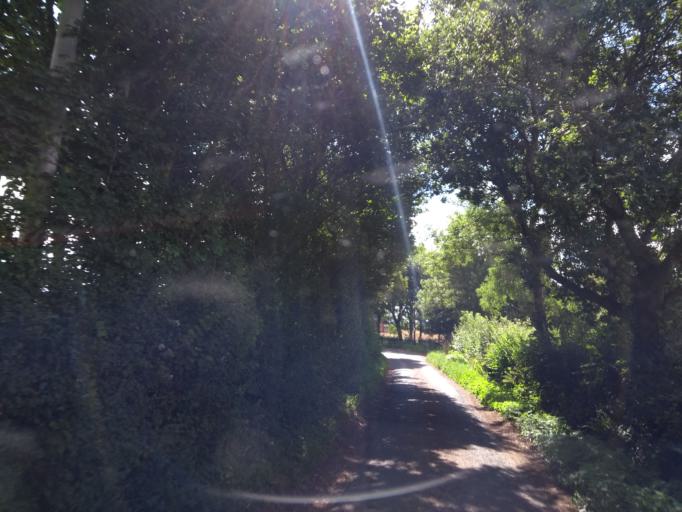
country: GB
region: England
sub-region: Somerset
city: Creech Saint Michael
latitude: 51.0390
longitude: -3.0224
